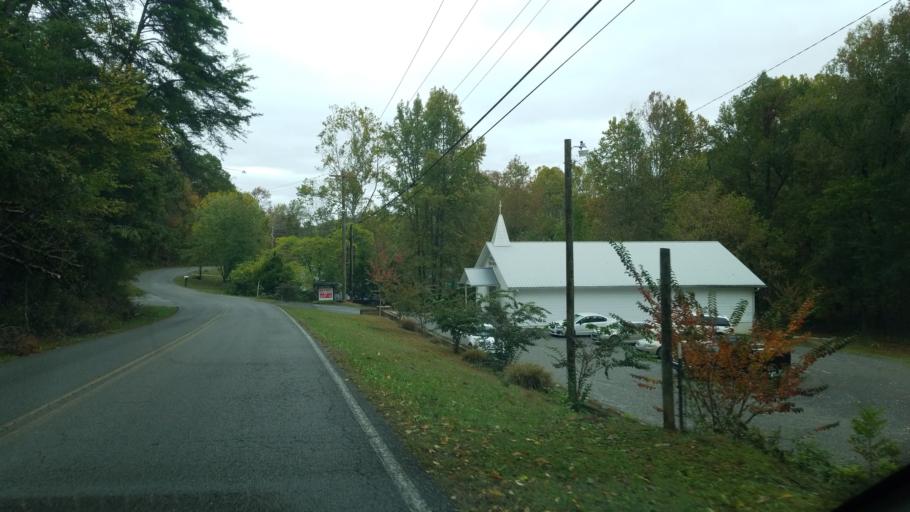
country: US
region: Tennessee
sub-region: Rhea County
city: Dayton
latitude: 35.5159
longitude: -85.0181
